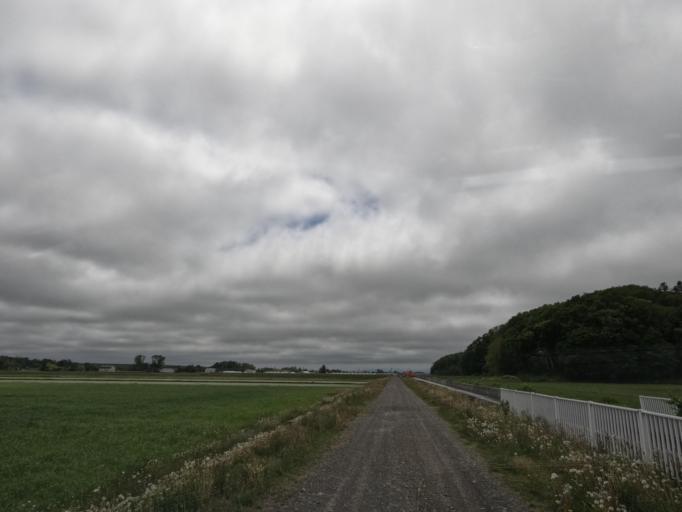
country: JP
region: Hokkaido
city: Tobetsu
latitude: 43.2696
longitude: 141.5238
